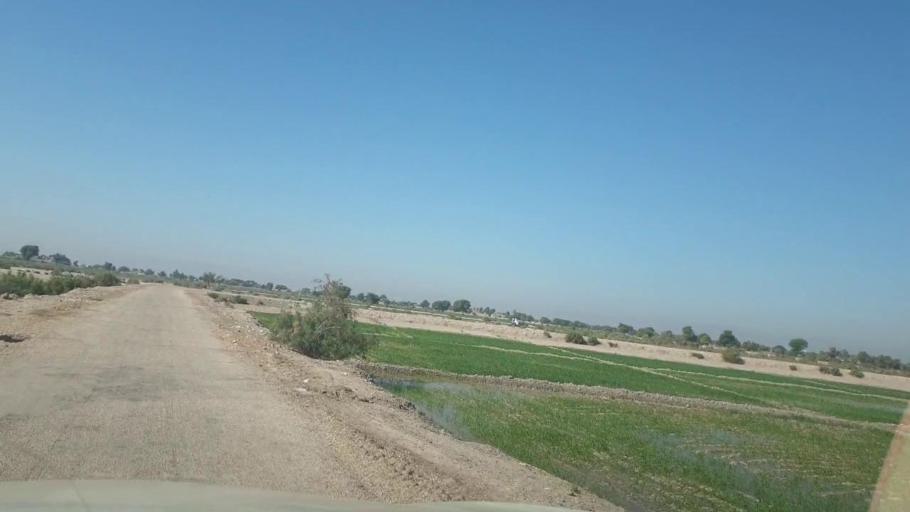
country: PK
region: Sindh
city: Bhan
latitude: 26.5399
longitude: 67.6452
